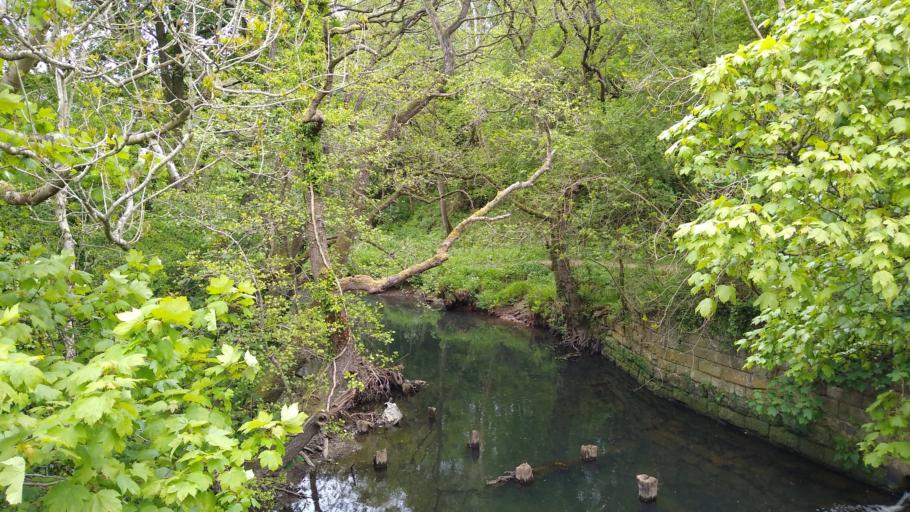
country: GB
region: England
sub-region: Cumbria
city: Dearham
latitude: 54.7209
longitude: -3.4466
